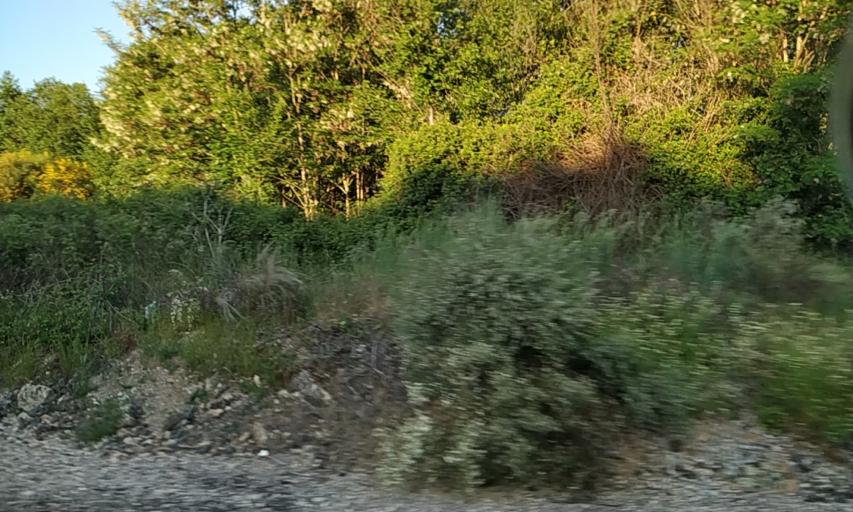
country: ES
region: Extremadura
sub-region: Provincia de Caceres
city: Valencia de Alcantara
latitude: 39.3871
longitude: -7.2475
